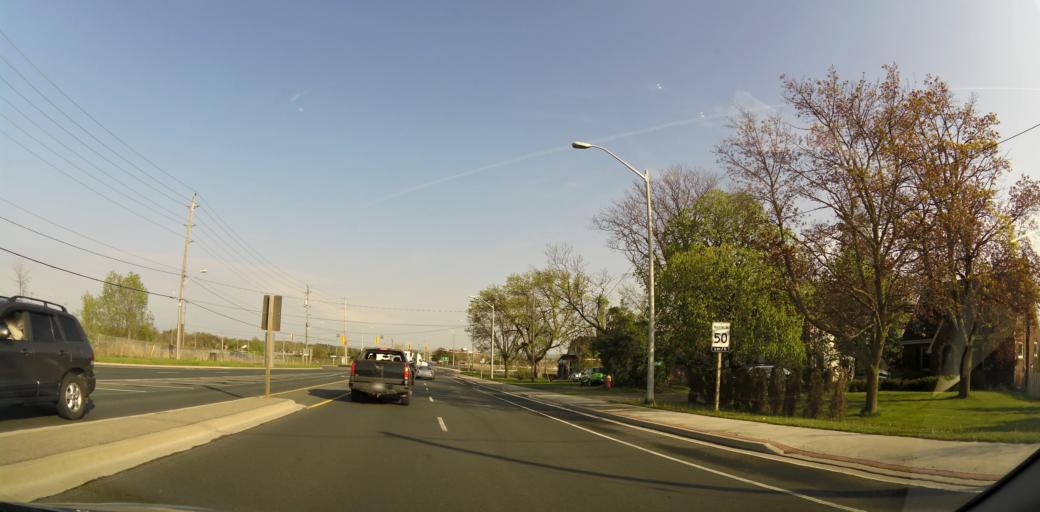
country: CA
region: Ontario
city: Hamilton
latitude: 43.3134
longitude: -79.8619
